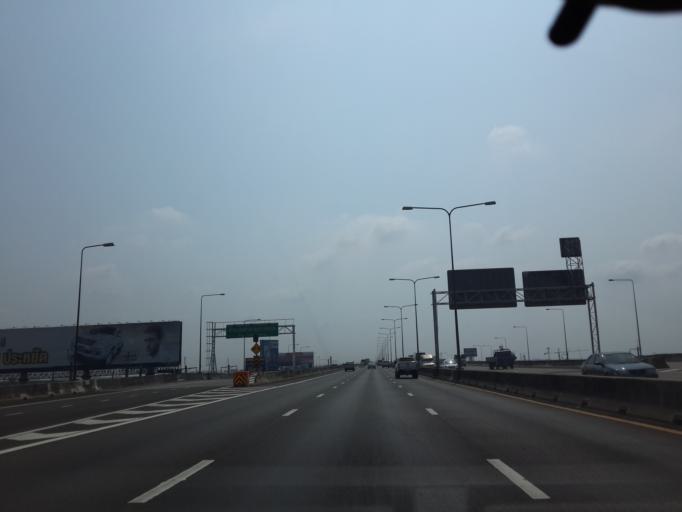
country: TH
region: Samut Prakan
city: Bang Bo District
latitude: 13.6243
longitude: 100.7299
